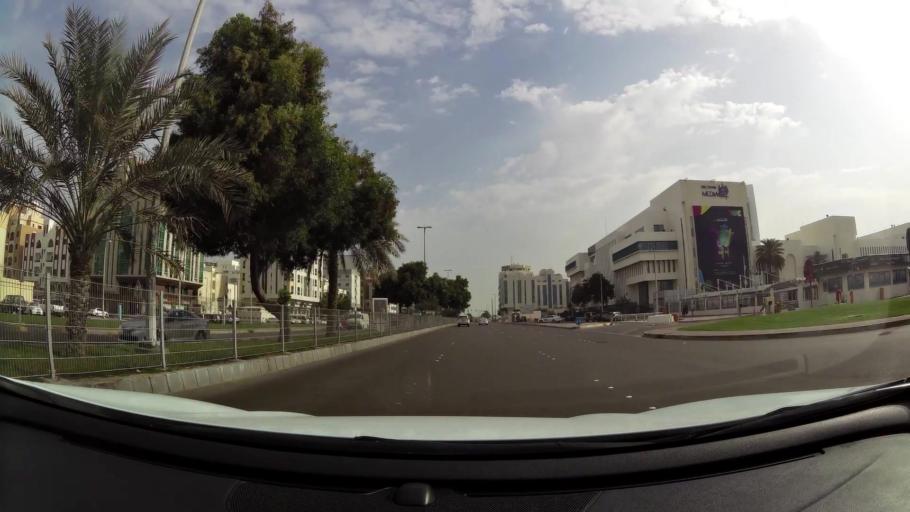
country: AE
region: Abu Dhabi
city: Abu Dhabi
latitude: 24.4595
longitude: 54.3846
